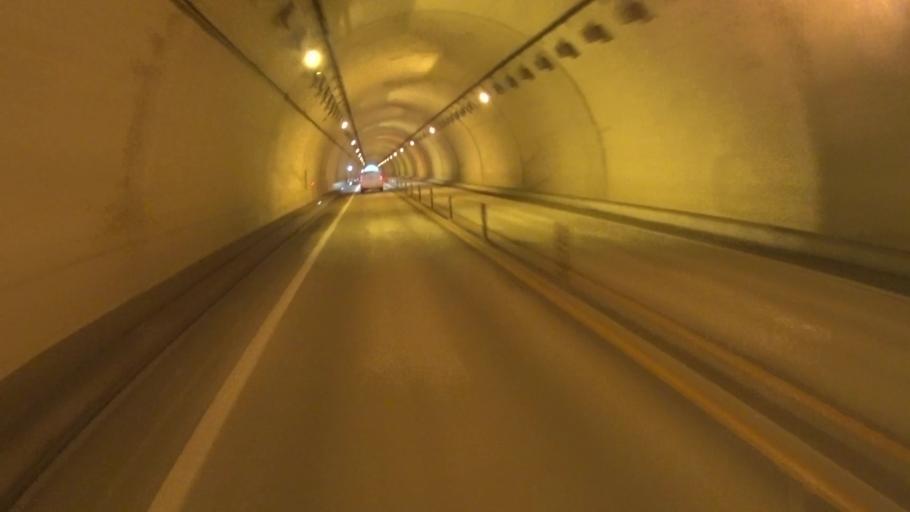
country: JP
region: Kyoto
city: Miyazu
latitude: 35.4607
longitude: 135.1752
